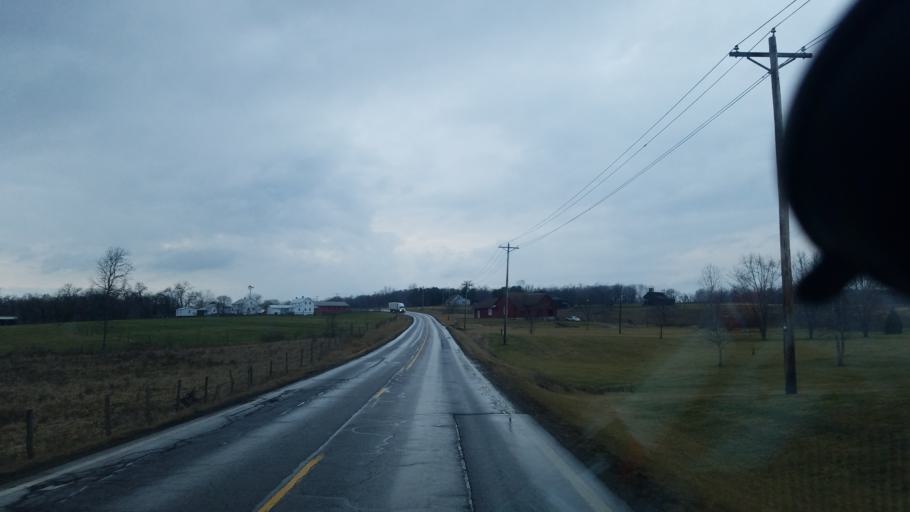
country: US
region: Ohio
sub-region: Knox County
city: Oak Hill
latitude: 40.3407
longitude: -82.2668
